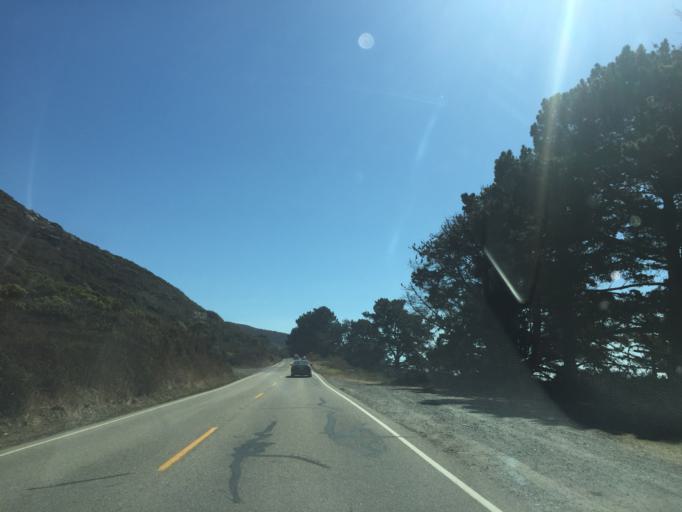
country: US
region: California
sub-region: Monterey County
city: Greenfield
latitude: 36.0589
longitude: -121.5907
